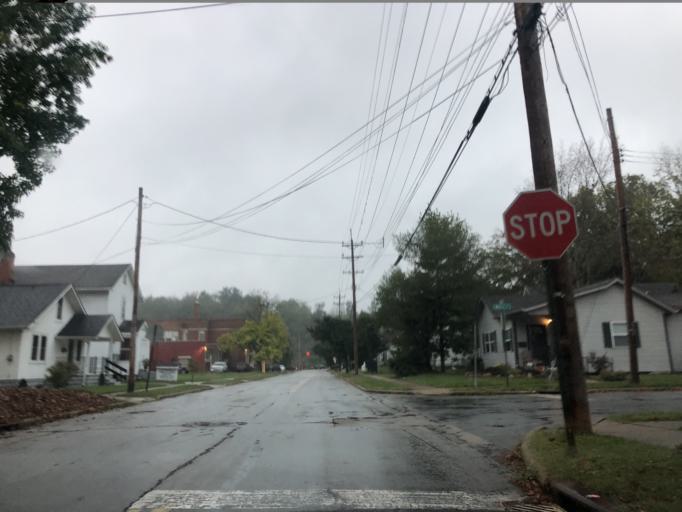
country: US
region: Ohio
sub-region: Hamilton County
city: Loveland
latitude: 39.2678
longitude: -84.2635
